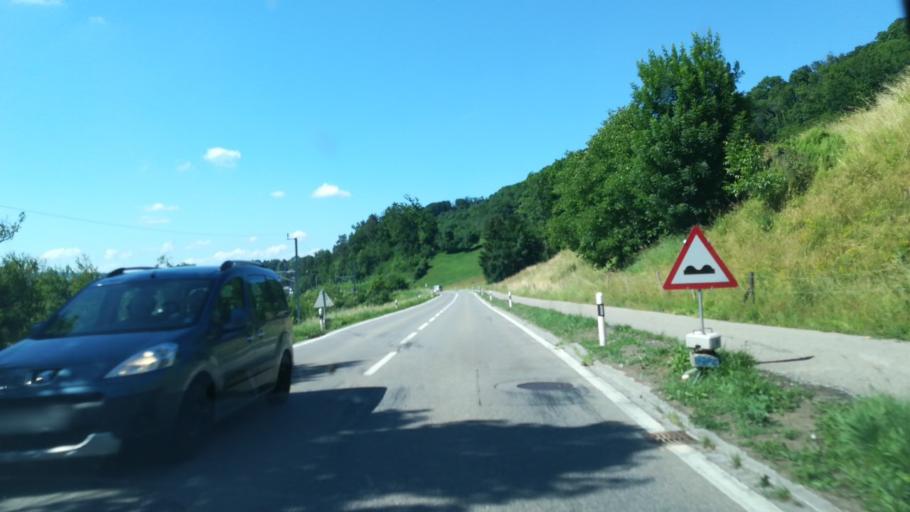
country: CH
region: Thurgau
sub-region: Weinfelden District
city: Sulgen
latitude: 47.5157
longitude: 9.2098
